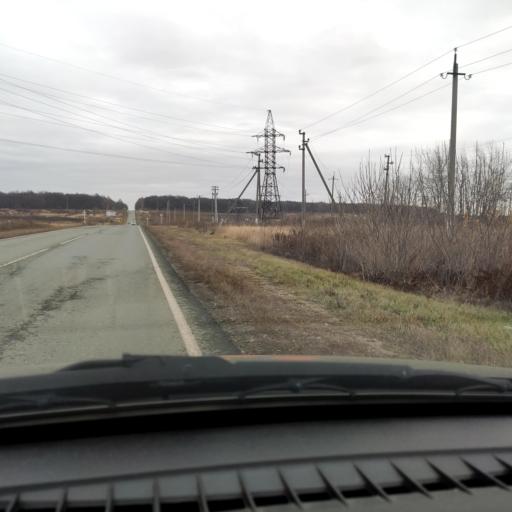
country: RU
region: Samara
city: Zhigulevsk
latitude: 53.3402
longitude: 49.4745
